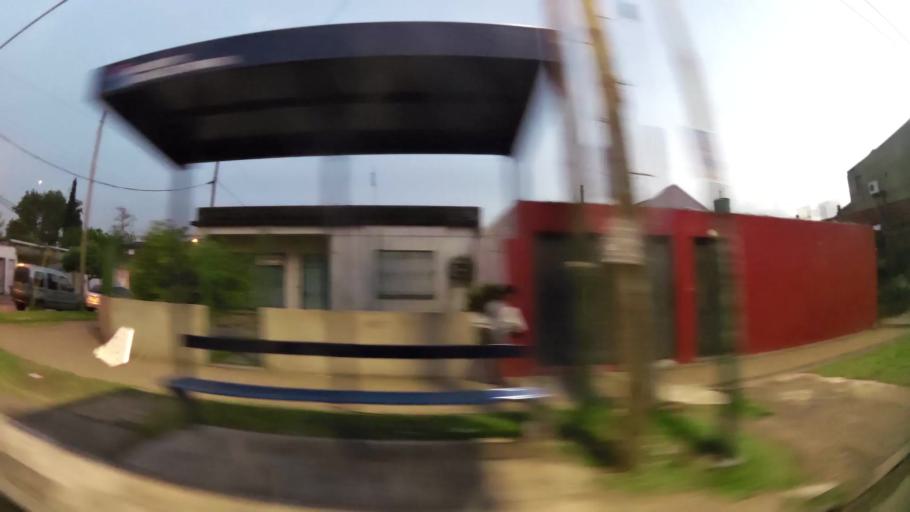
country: AR
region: Buenos Aires
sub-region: Partido de Lomas de Zamora
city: Lomas de Zamora
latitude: -34.7480
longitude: -58.3608
